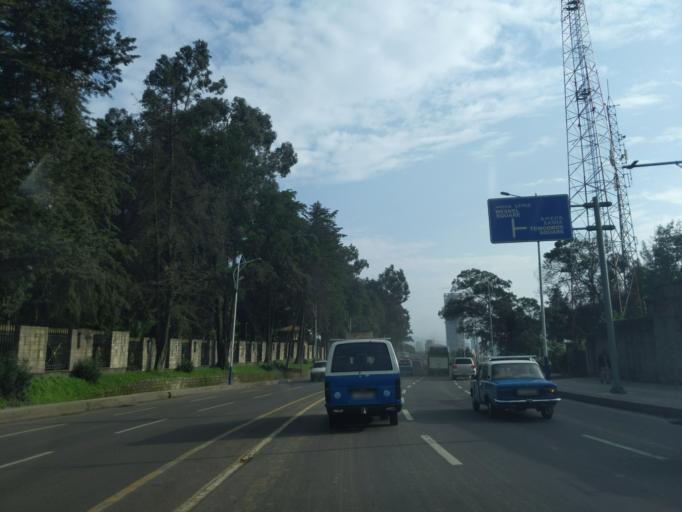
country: ET
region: Adis Abeba
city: Addis Ababa
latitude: 9.0275
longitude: 38.7630
